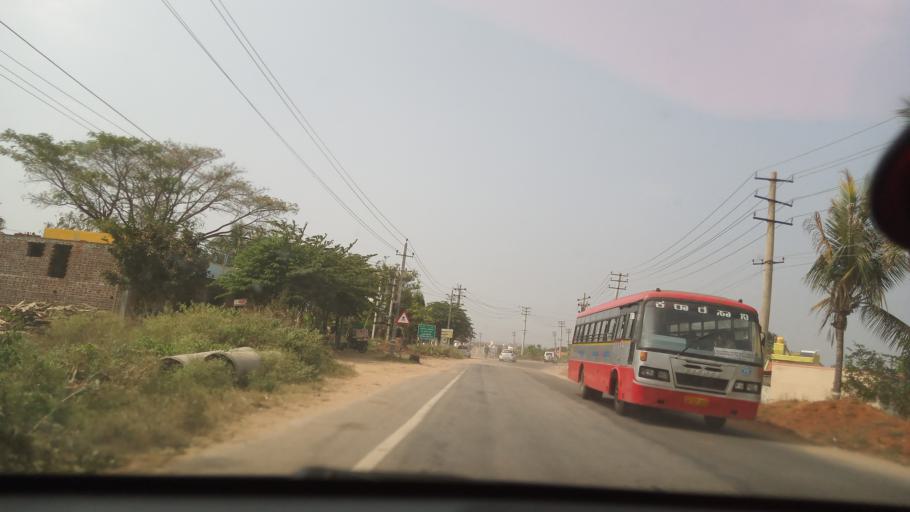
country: IN
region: Karnataka
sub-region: Chamrajnagar
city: Chamrajnagar
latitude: 11.9864
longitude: 76.8722
